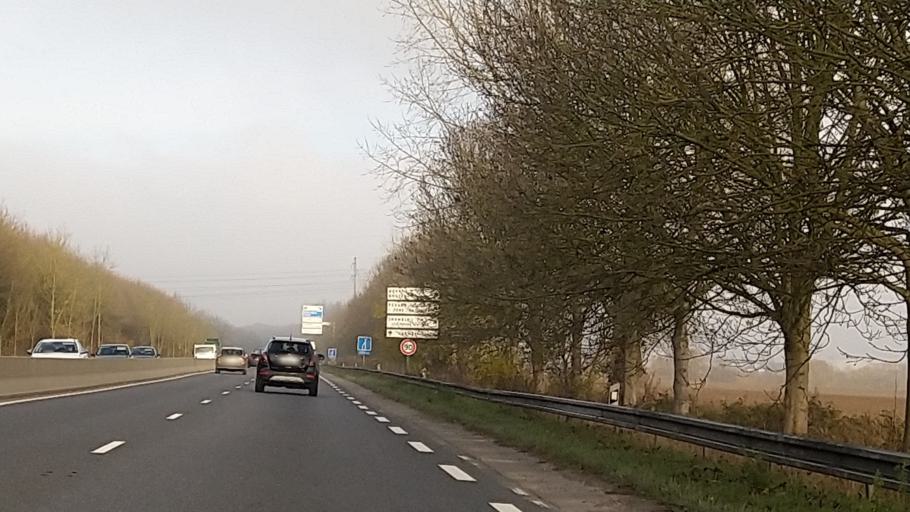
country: FR
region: Ile-de-France
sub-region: Departement du Val-d'Oise
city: Champagne-sur-Oise
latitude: 49.1446
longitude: 2.2506
